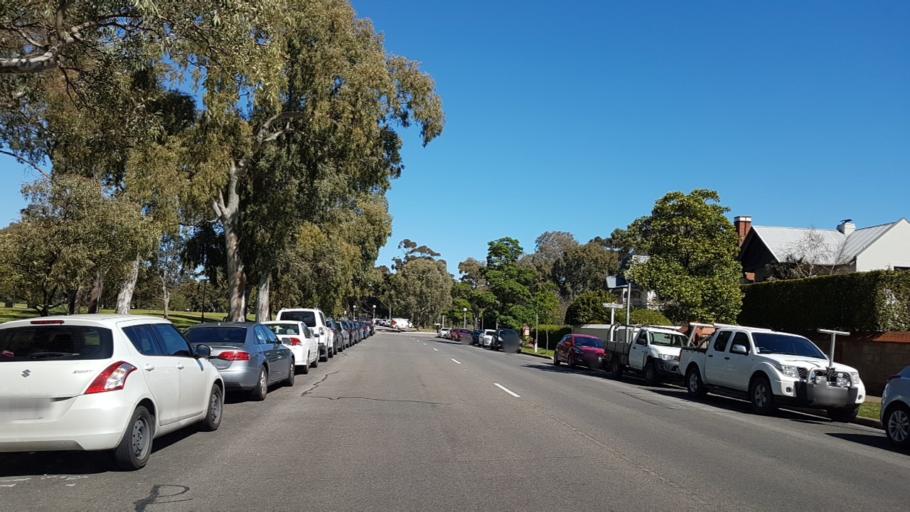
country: AU
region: South Australia
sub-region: Adelaide
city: Adelaide
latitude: -34.9337
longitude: 138.6178
